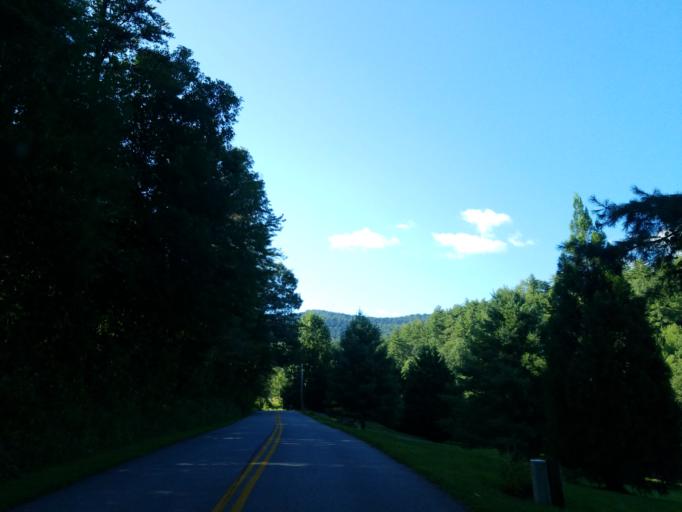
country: US
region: Georgia
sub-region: Union County
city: Blairsville
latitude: 34.7528
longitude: -84.1143
